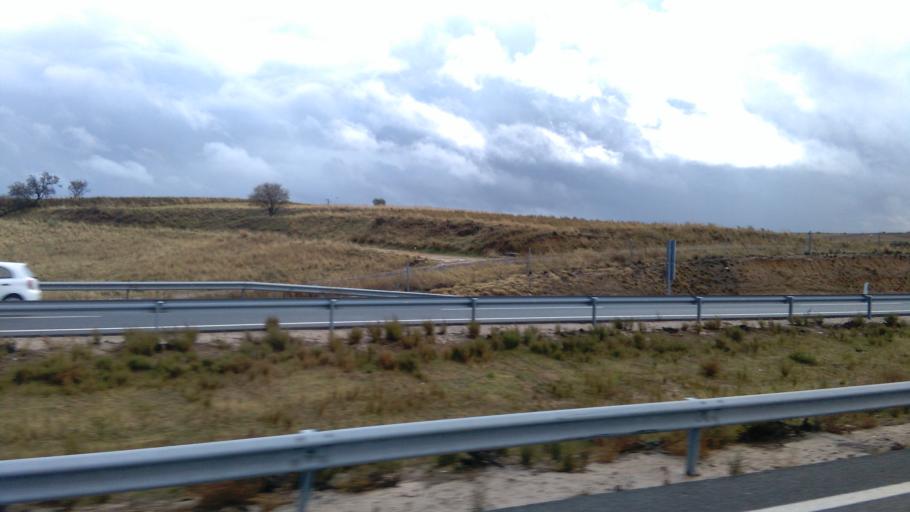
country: ES
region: Castille-La Mancha
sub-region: Province of Toledo
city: Valmojado
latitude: 40.2020
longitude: -4.1042
